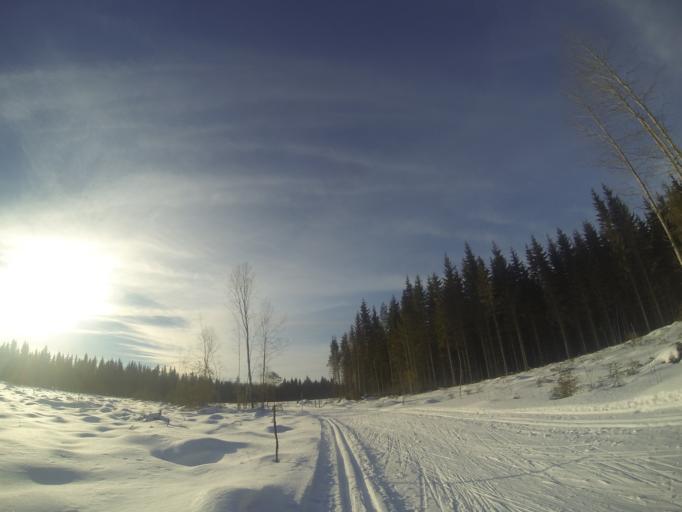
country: FI
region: Southern Savonia
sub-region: Savonlinna
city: Savonlinna
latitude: 61.9361
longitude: 28.9138
